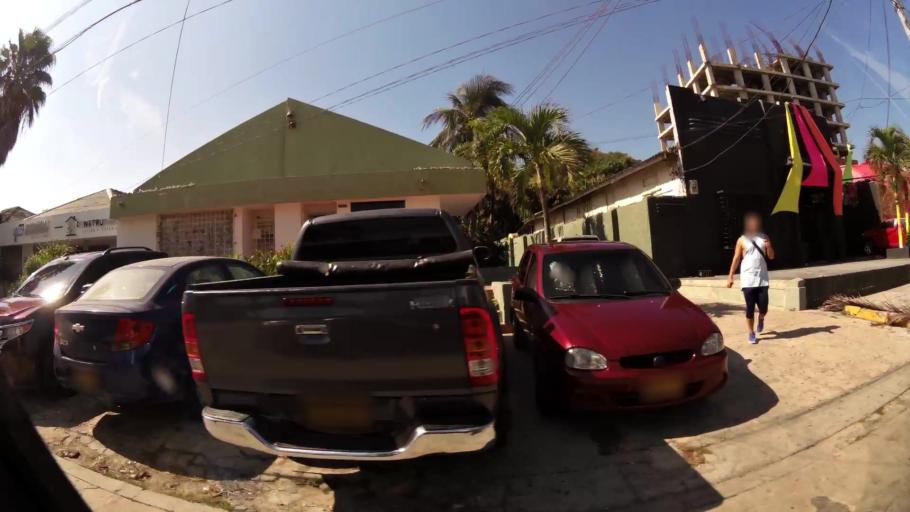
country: CO
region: Atlantico
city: Barranquilla
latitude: 10.9972
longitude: -74.8056
